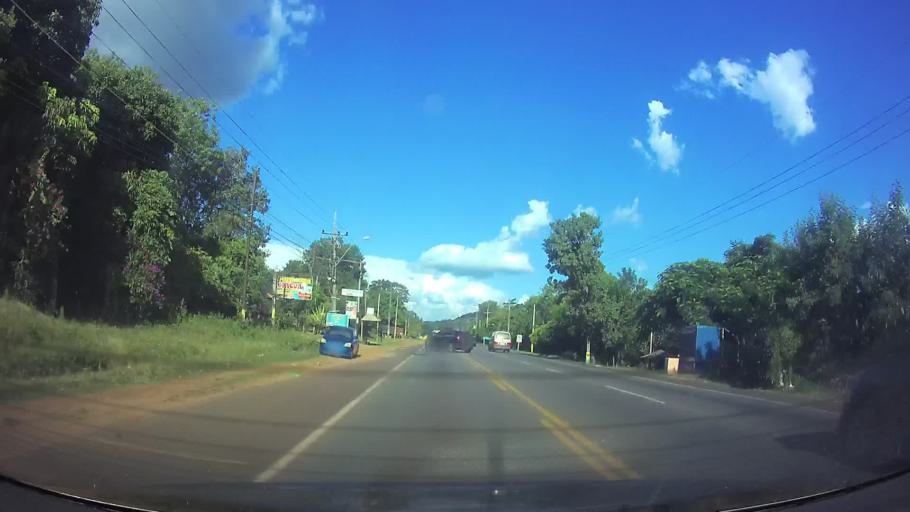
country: PY
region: Cordillera
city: Caacupe
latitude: -25.3881
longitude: -57.1106
